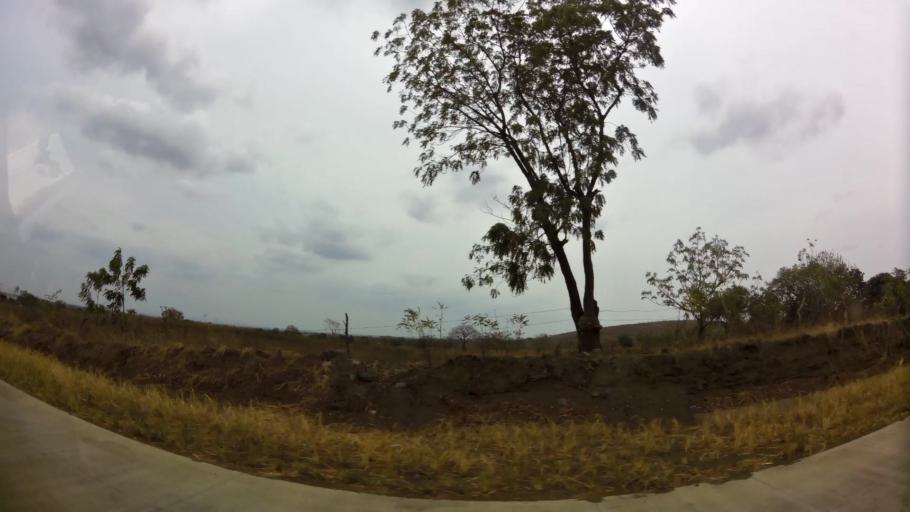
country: NI
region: Managua
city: Managua
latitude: 12.0994
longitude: -86.1766
